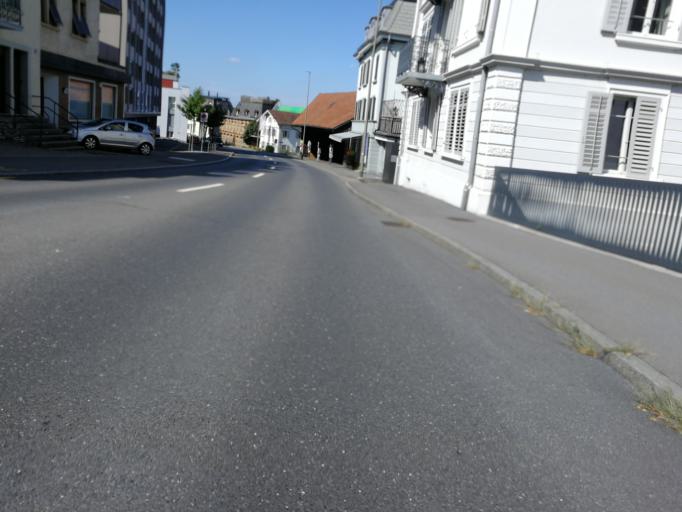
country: CH
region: Zurich
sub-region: Bezirk Horgen
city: Horgen / Horgen (Dorfkern)
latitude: 47.2568
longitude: 8.6017
